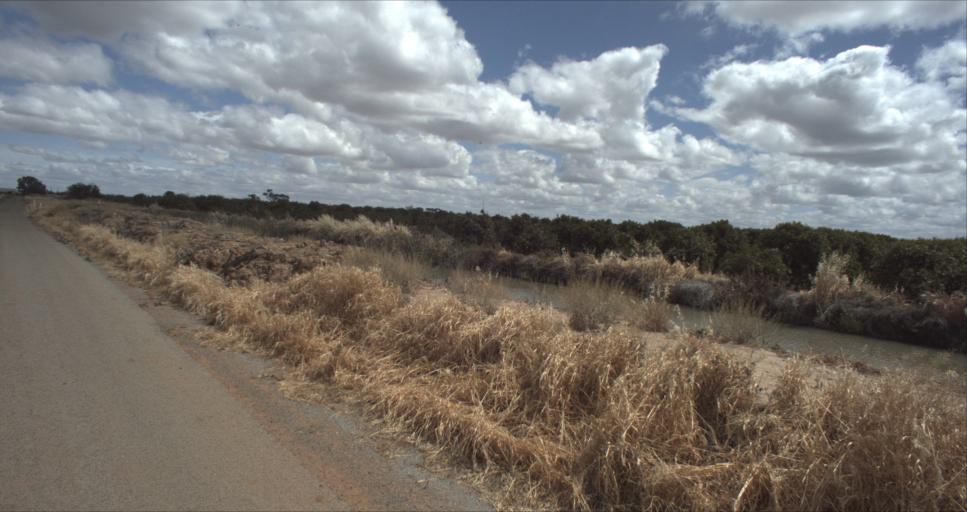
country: AU
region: New South Wales
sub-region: Leeton
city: Leeton
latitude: -34.5849
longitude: 146.3915
